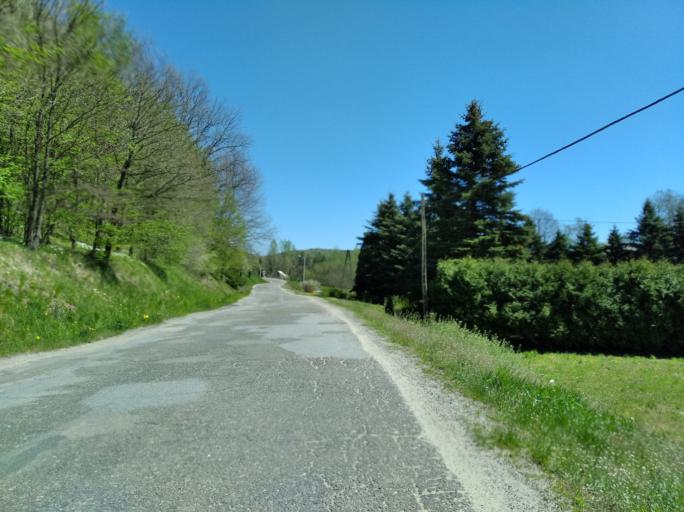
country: PL
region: Subcarpathian Voivodeship
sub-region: Powiat debicki
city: Brzostek
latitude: 49.9104
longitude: 21.4746
